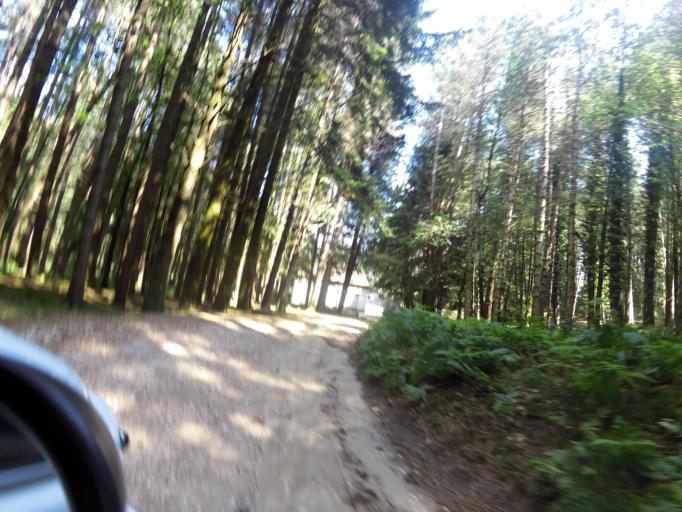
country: IT
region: Calabria
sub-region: Provincia di Vibo-Valentia
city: Nardodipace
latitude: 38.5098
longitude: 16.3779
